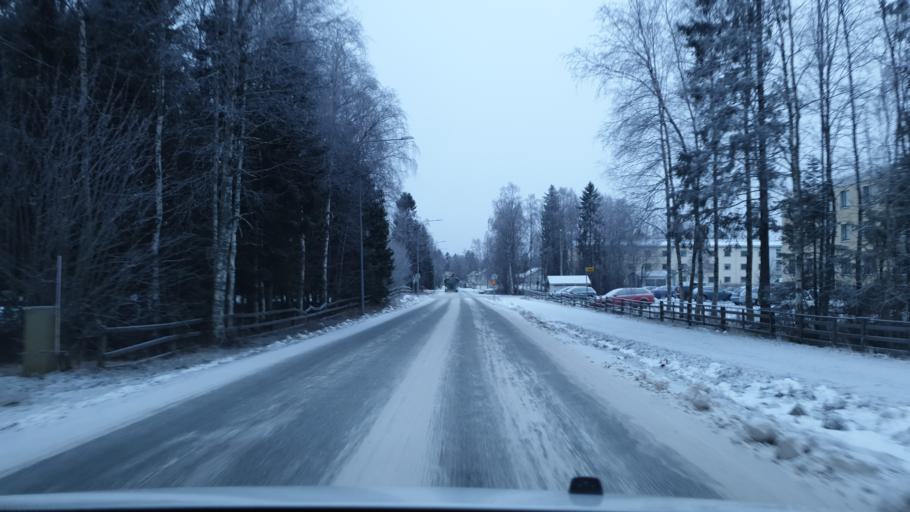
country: FI
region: Lapland
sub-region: Kemi-Tornio
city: Kemi
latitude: 65.7349
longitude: 24.6090
